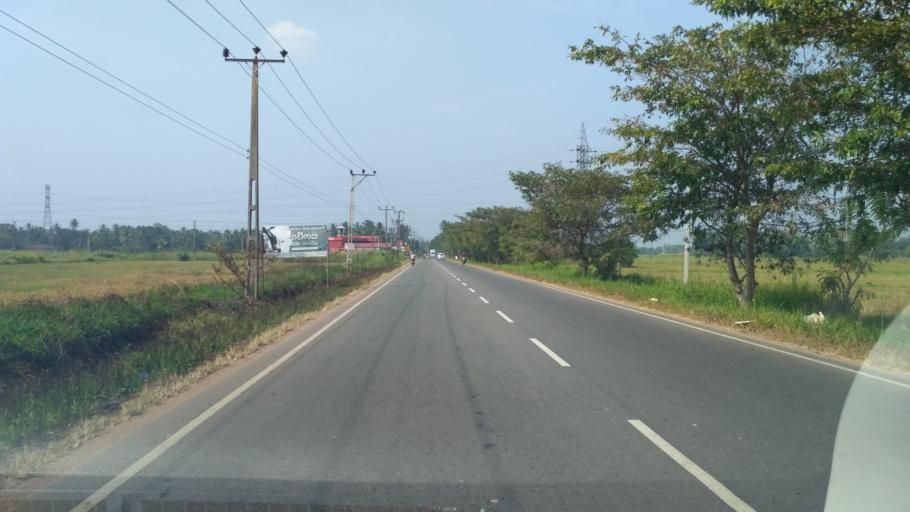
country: LK
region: North Western
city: Kuliyapitiya
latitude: 7.3288
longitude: 79.9947
